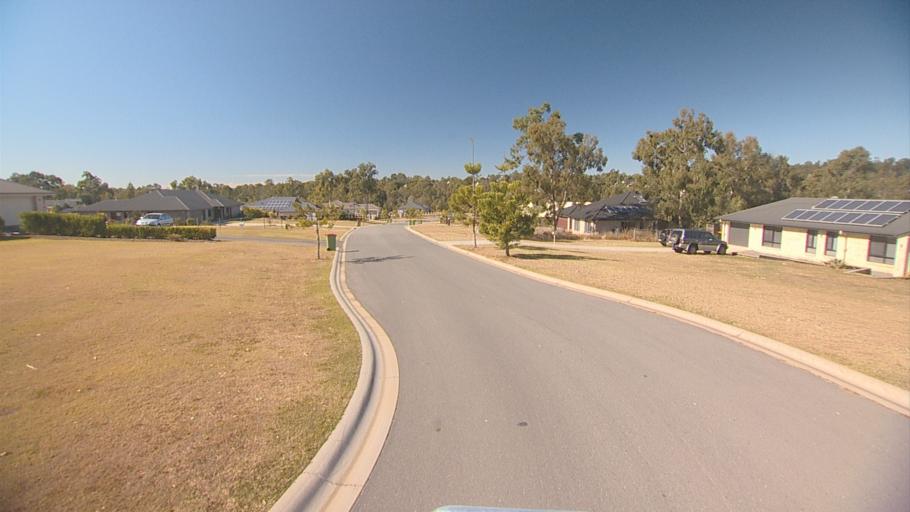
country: AU
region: Queensland
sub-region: Logan
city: North Maclean
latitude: -27.7531
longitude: 152.9496
